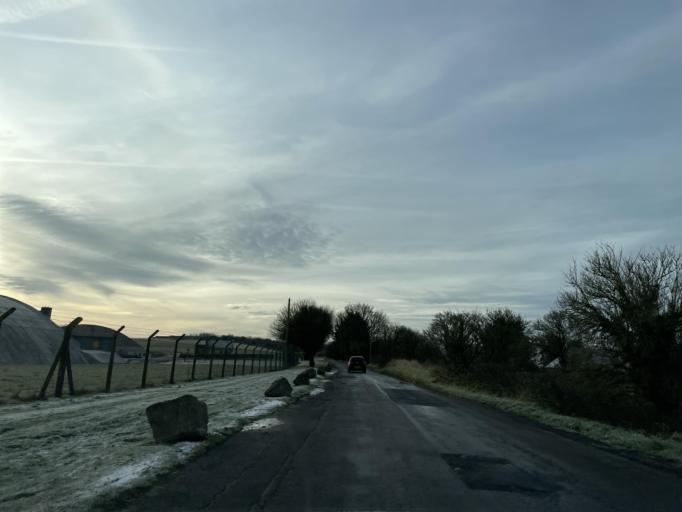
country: GB
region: England
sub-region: Borough of Swindon
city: Wroughton
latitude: 51.5120
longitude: -1.8128
